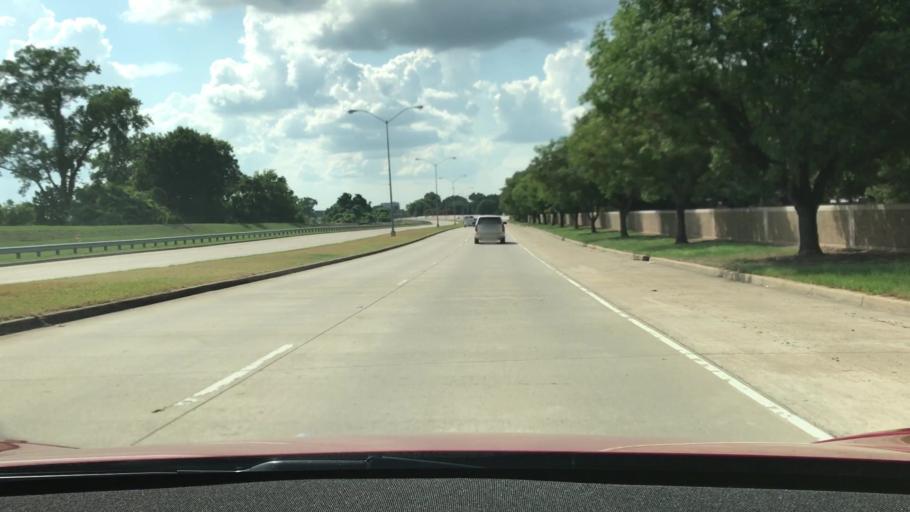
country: US
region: Louisiana
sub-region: Bossier Parish
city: Bossier City
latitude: 32.5072
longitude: -93.7131
